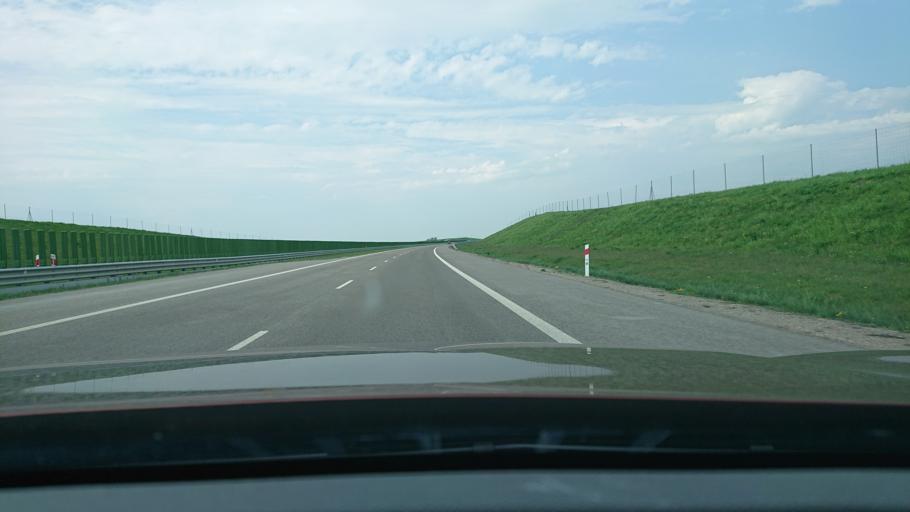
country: PL
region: Subcarpathian Voivodeship
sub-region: Powiat jaroslawski
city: Pawlosiow
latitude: 49.9477
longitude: 22.6654
